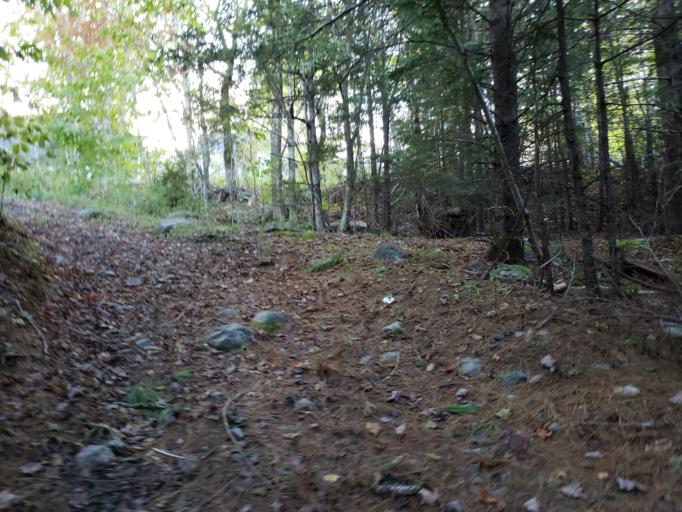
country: CA
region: Nova Scotia
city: Cole Harbour
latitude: 44.7440
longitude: -63.3804
